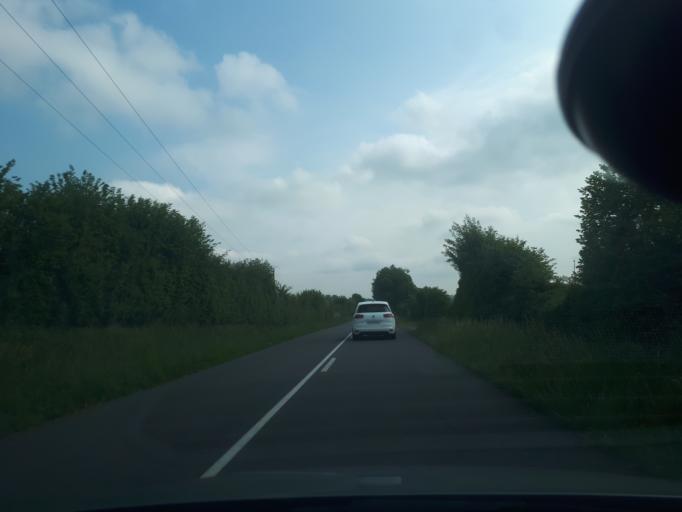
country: FR
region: Auvergne
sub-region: Departement de l'Allier
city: Dompierre-sur-Besbre
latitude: 46.4150
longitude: 3.6098
